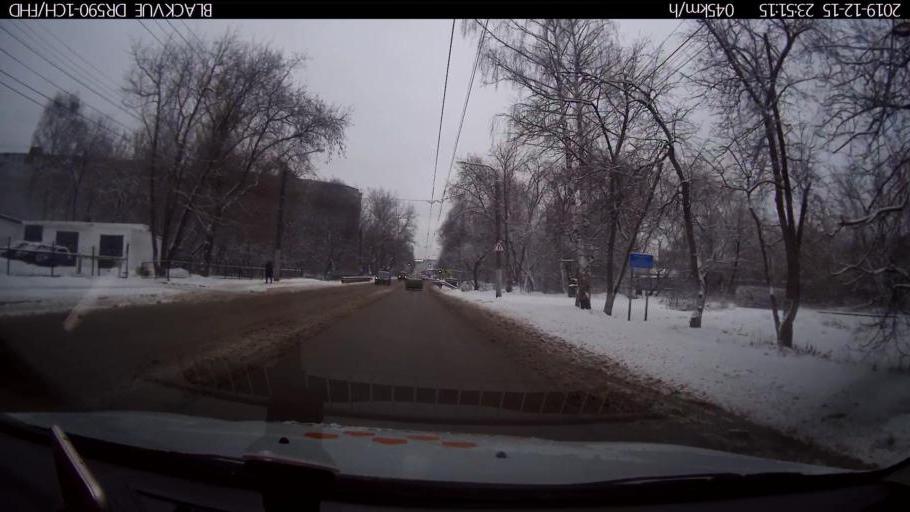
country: RU
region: Nizjnij Novgorod
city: Nizhniy Novgorod
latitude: 56.2755
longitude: 43.9358
